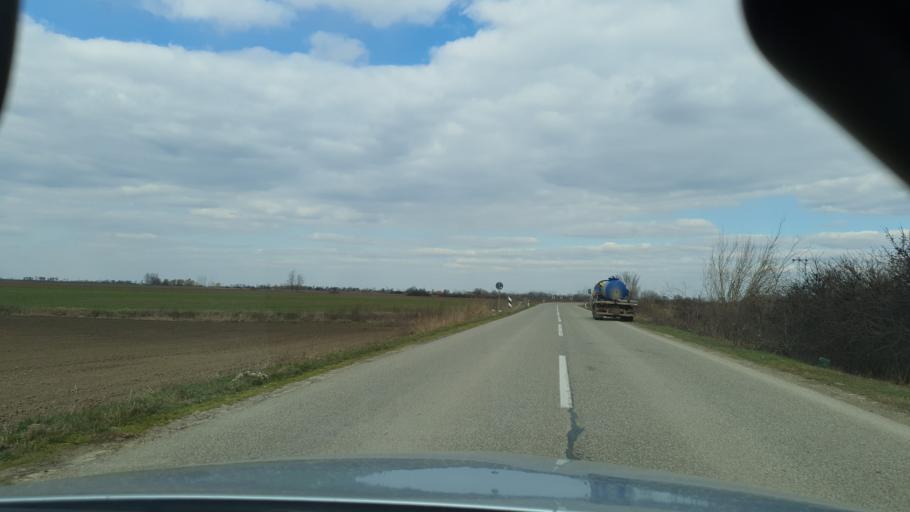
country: RS
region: Autonomna Pokrajina Vojvodina
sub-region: Zapadnobacki Okrug
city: Odzaci
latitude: 45.4407
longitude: 19.3159
